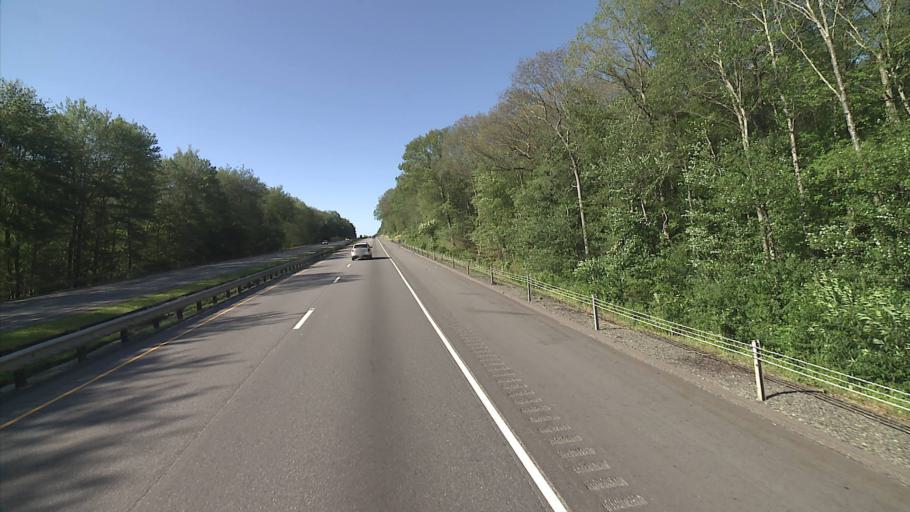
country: US
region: Connecticut
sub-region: New London County
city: Oxoboxo River
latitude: 41.4550
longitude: -72.1164
